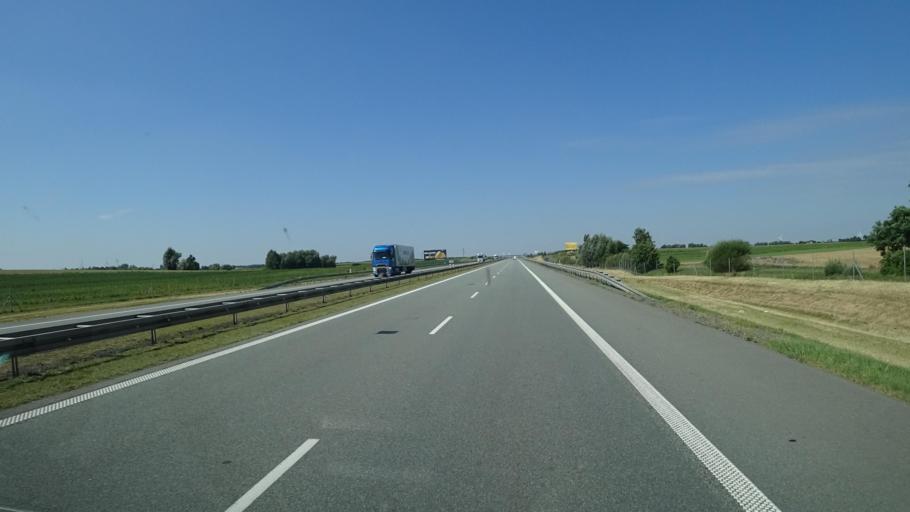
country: PL
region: Greater Poland Voivodeship
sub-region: Powiat wrzesinski
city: Nekla
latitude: 52.3189
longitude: 17.4626
